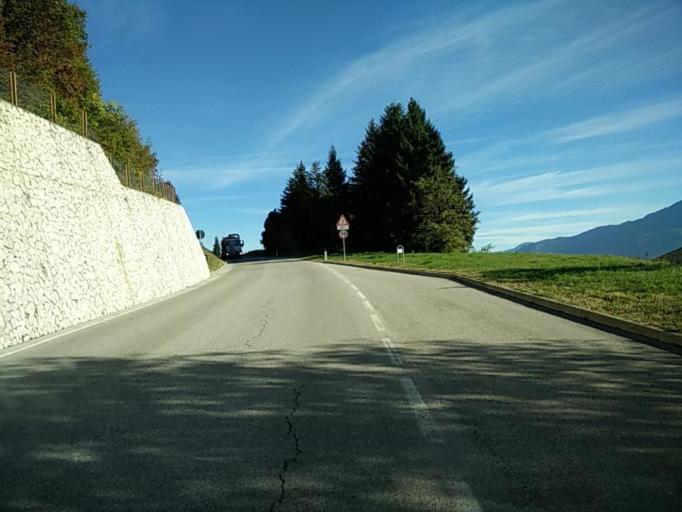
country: IT
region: Trentino-Alto Adige
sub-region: Provincia di Trento
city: Cimoneri
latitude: 45.9878
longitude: 11.0827
